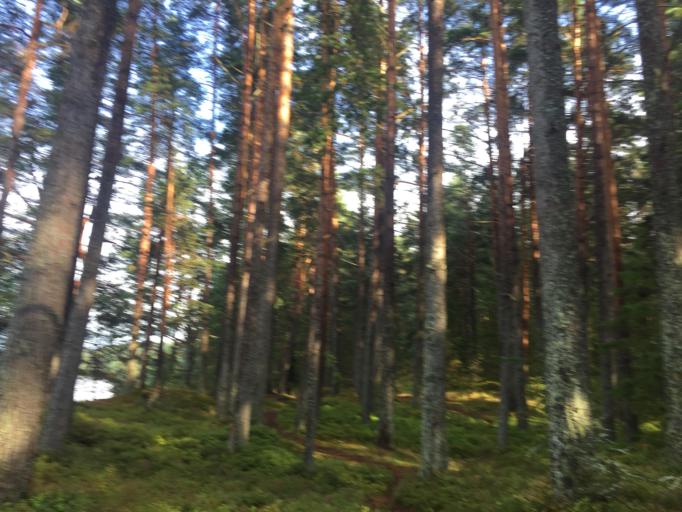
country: RU
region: Leningrad
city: Priozersk
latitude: 60.9766
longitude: 30.2898
